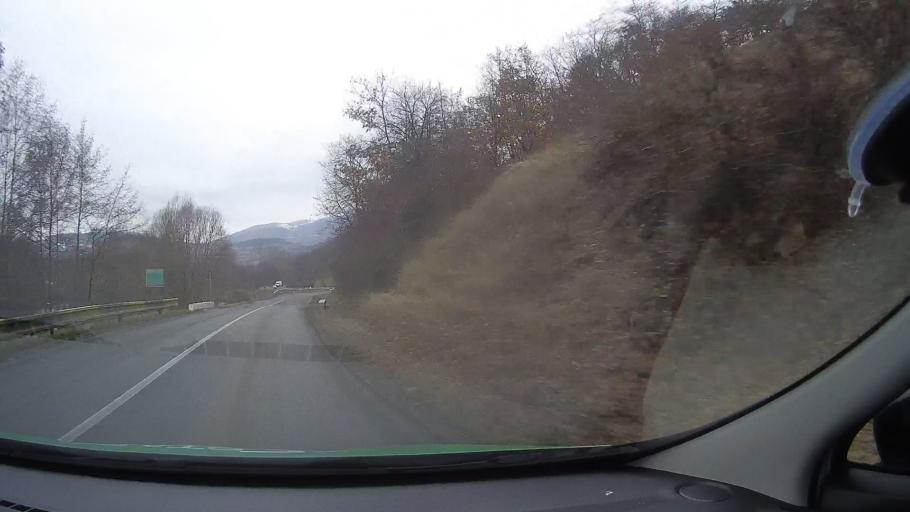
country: RO
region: Alba
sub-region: Comuna Metes
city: Metes
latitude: 46.1023
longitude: 23.4540
